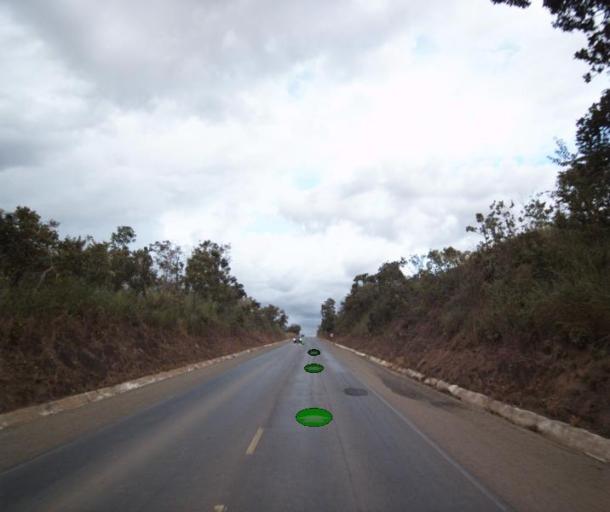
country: BR
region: Goias
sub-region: Uruacu
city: Uruacu
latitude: -14.7752
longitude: -49.2688
